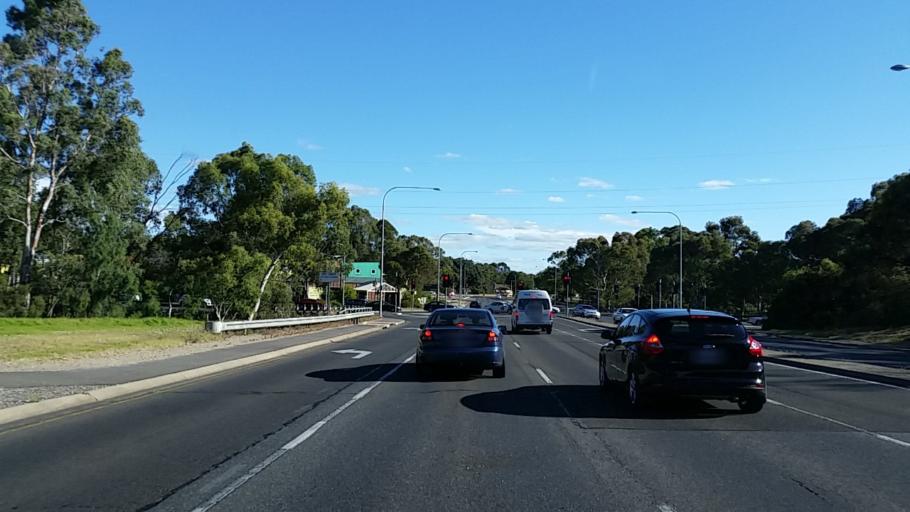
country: AU
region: South Australia
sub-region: Tea Tree Gully
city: Modbury
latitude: -34.8330
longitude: 138.6804
